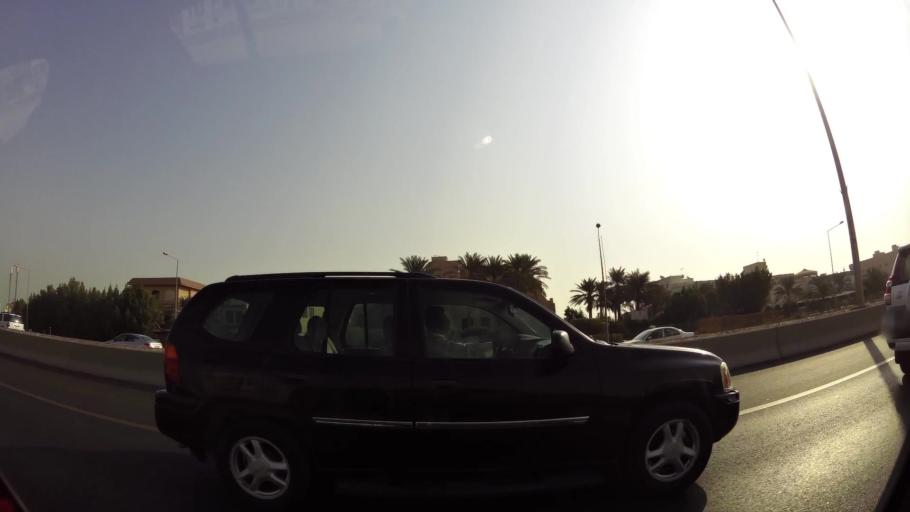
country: KW
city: Al Funaytis
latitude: 29.2245
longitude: 48.0994
